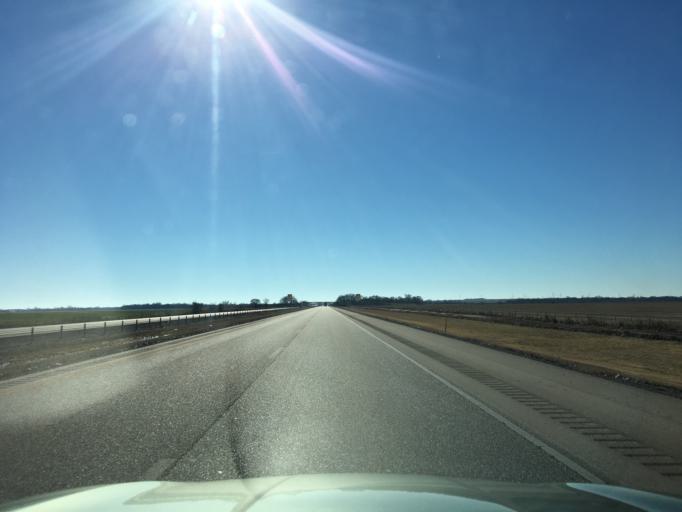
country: US
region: Oklahoma
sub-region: Kay County
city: Blackwell
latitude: 36.9209
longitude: -97.3505
